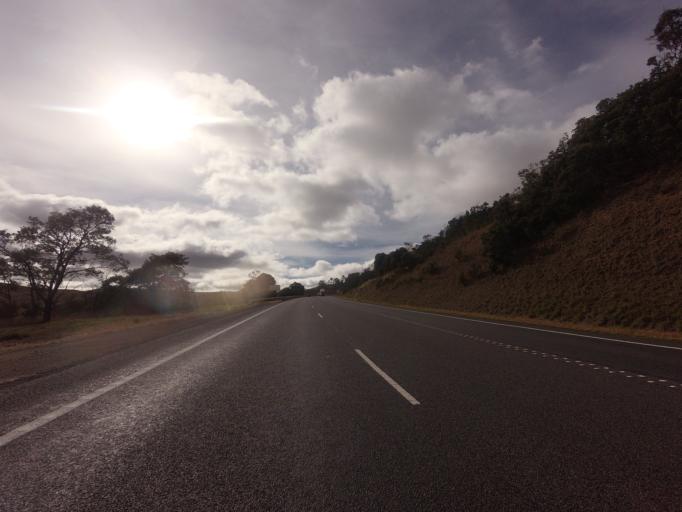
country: AU
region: Tasmania
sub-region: Brighton
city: Bridgewater
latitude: -42.4139
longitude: 147.2619
